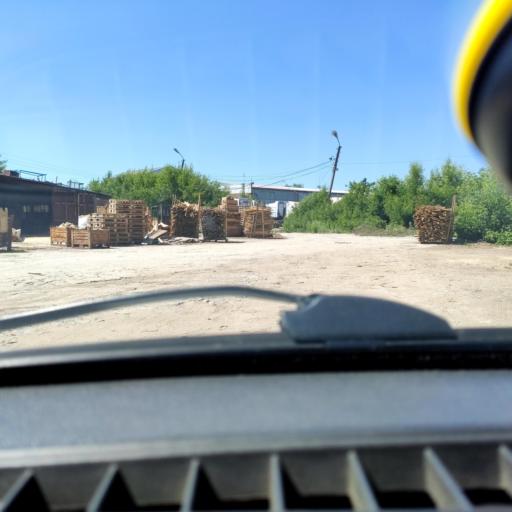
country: RU
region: Samara
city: Tol'yatti
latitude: 53.5694
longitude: 49.2993
